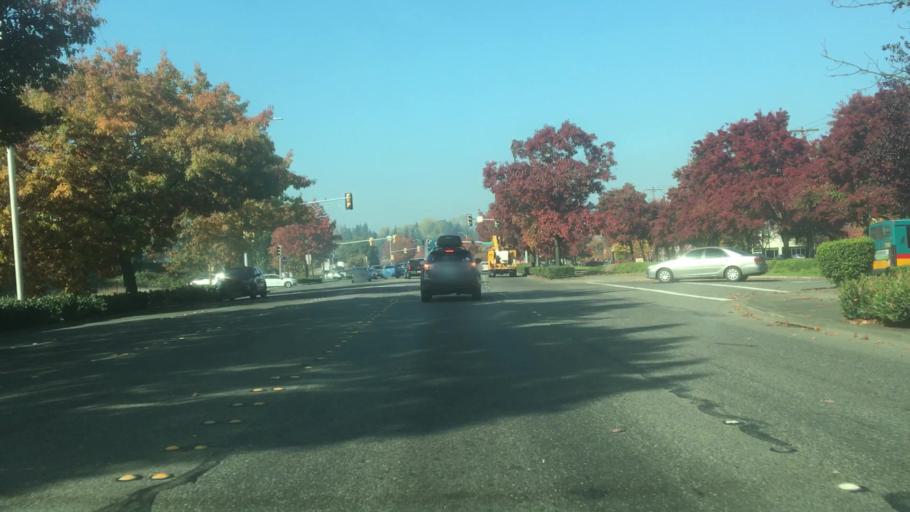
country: US
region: Washington
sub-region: King County
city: Tukwila
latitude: 47.4853
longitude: -122.2733
